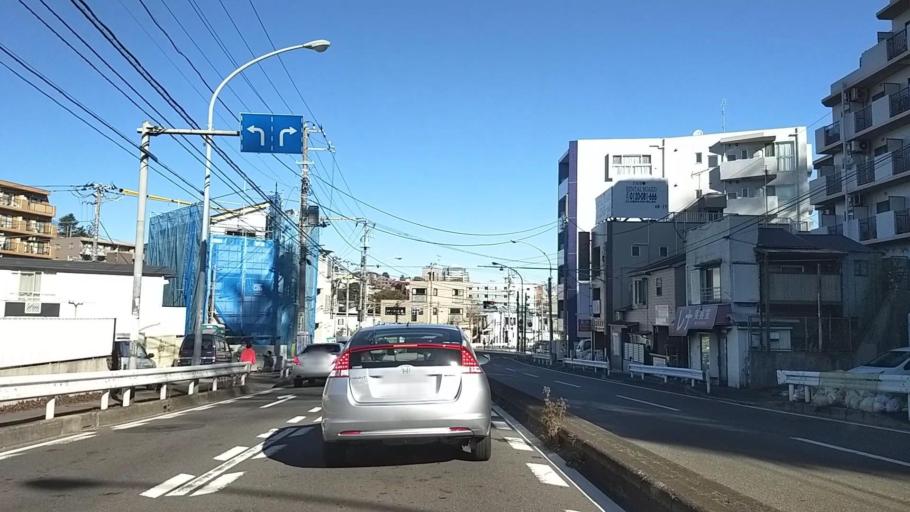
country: JP
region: Kanagawa
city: Yokohama
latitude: 35.4429
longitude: 139.5962
